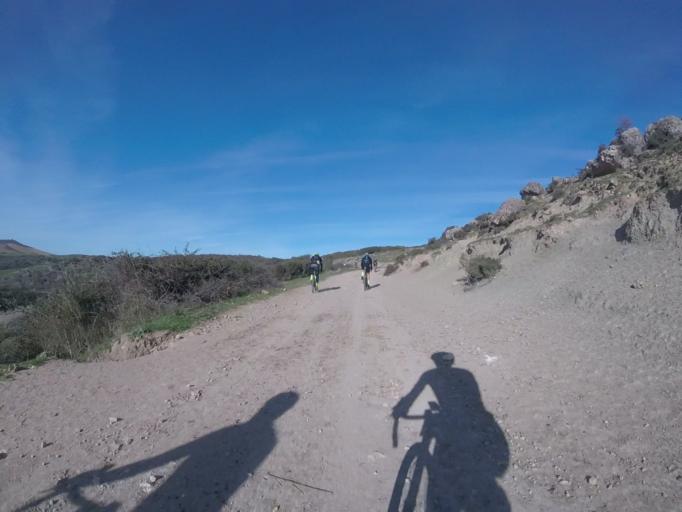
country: ES
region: Navarre
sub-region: Provincia de Navarra
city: Yerri
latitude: 42.6963
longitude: -1.9596
